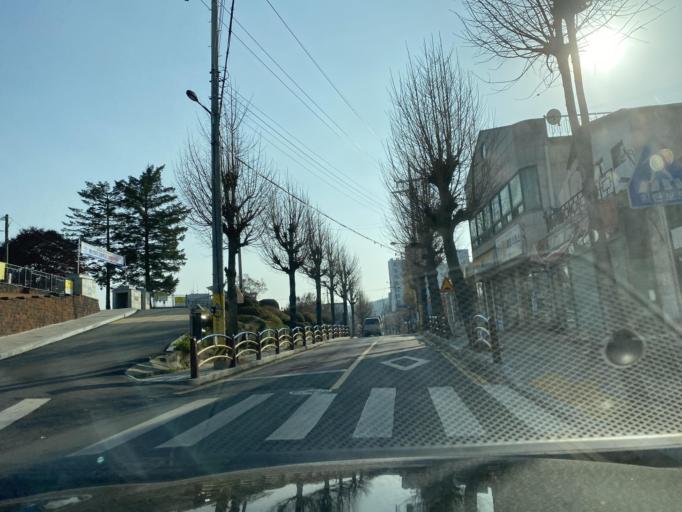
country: KR
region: Chungcheongnam-do
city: Yesan
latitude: 36.6851
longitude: 126.8327
